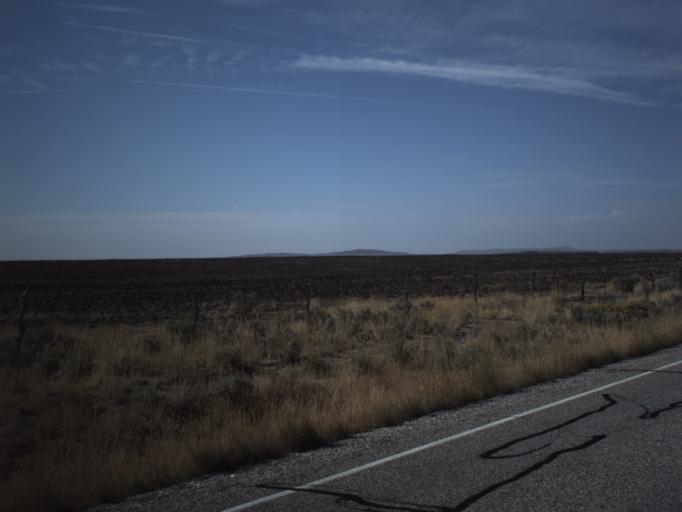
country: US
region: Idaho
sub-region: Minidoka County
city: Rupert
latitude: 41.8301
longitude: -113.1634
